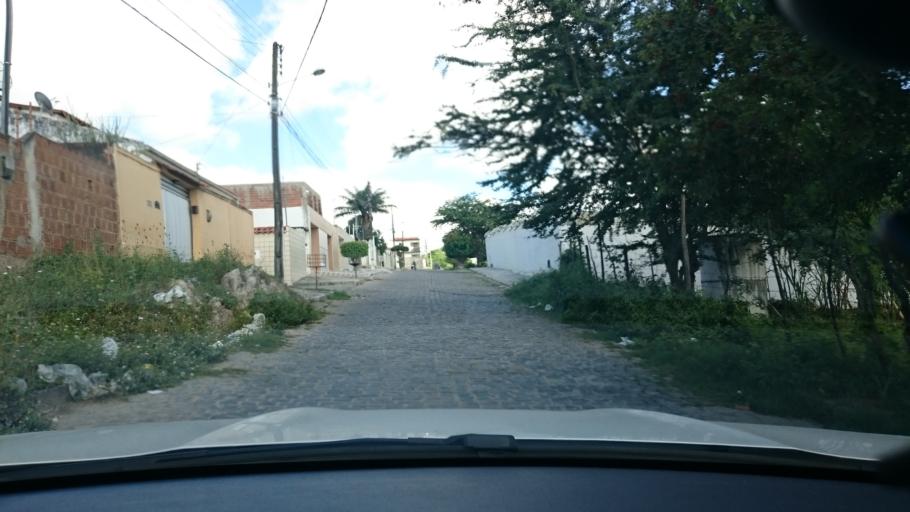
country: BR
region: Paraiba
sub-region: Campina Grande
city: Campina Grande
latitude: -7.2380
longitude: -35.9241
